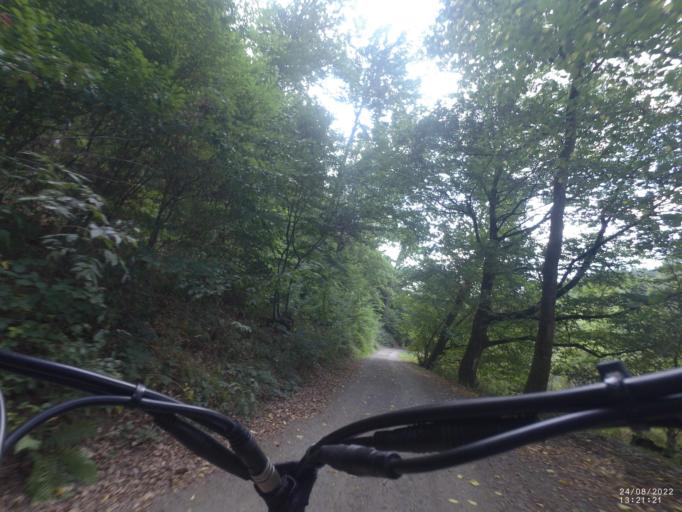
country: DE
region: Rheinland-Pfalz
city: Neroth
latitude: 50.1898
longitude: 6.7506
